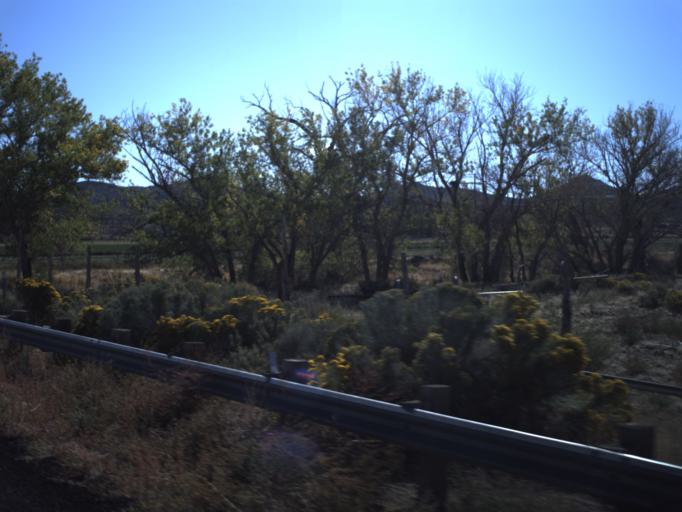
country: US
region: Utah
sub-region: Washington County
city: Enterprise
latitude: 37.6728
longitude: -113.5412
